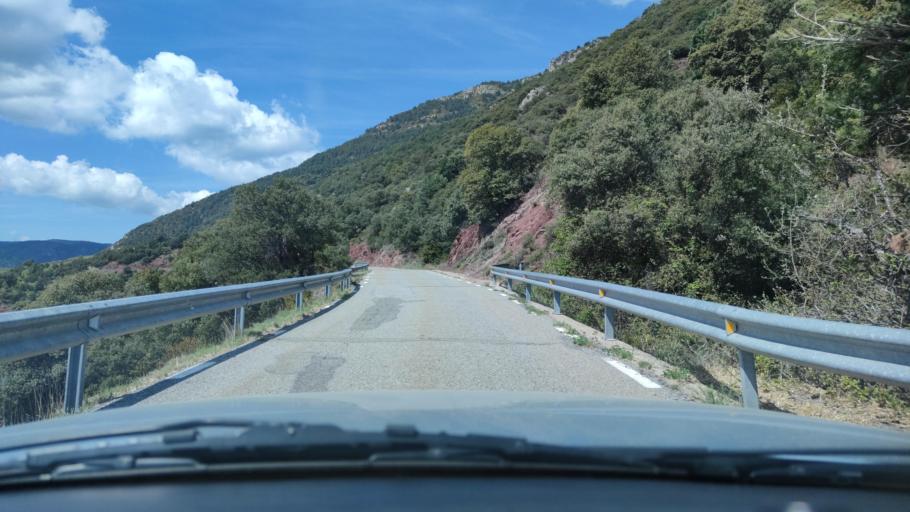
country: ES
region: Catalonia
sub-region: Provincia de Lleida
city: Coll de Nargo
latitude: 42.3018
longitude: 1.2824
